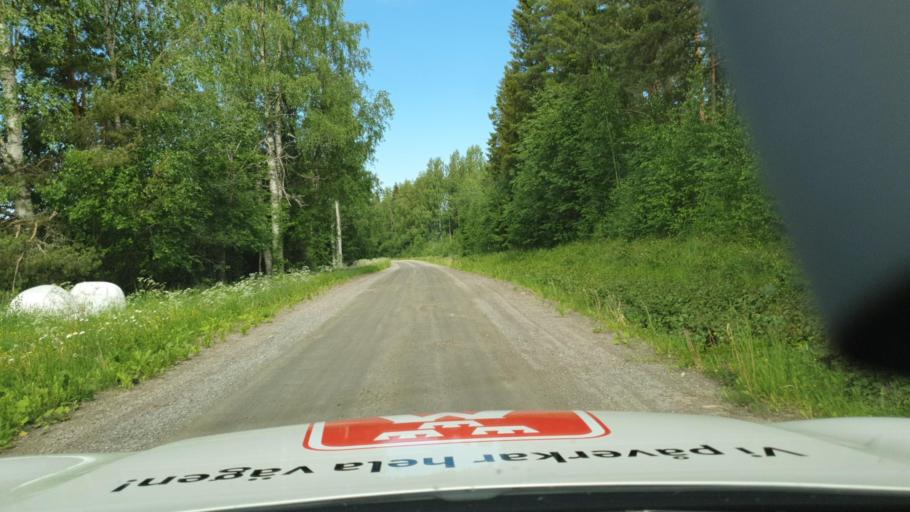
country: SE
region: Vaesterbotten
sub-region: Skelleftea Kommun
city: Forsbacka
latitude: 64.6746
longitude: 20.5293
